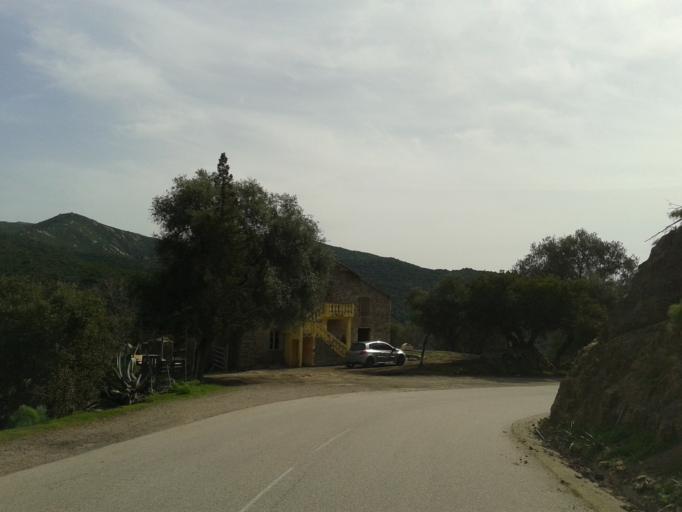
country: FR
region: Corsica
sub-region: Departement de la Haute-Corse
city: Monticello
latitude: 42.6556
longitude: 9.1156
